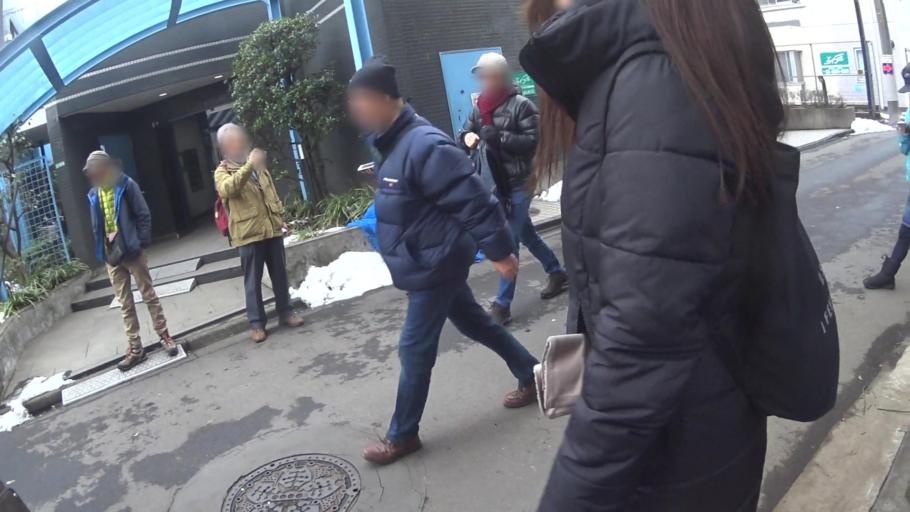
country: JP
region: Tokyo
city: Musashino
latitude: 35.7281
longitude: 139.5999
